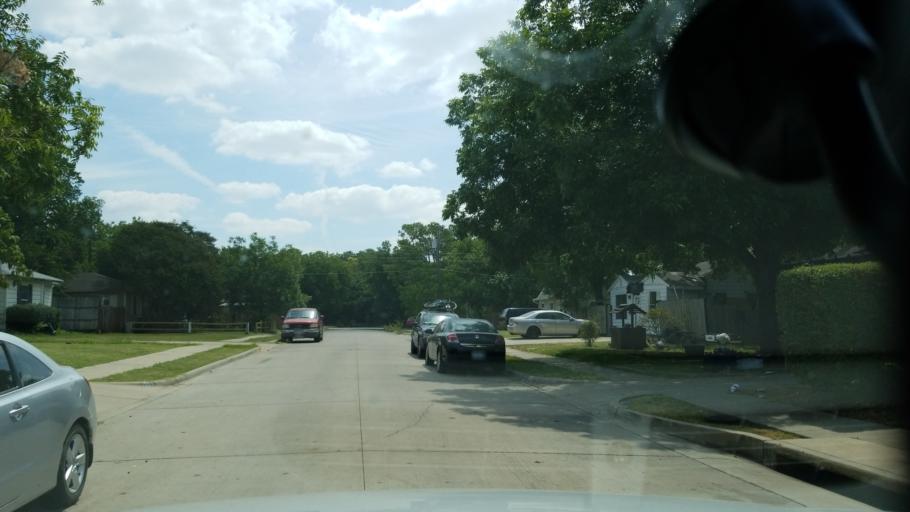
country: US
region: Texas
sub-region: Dallas County
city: Grand Prairie
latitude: 32.7538
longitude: -96.9821
